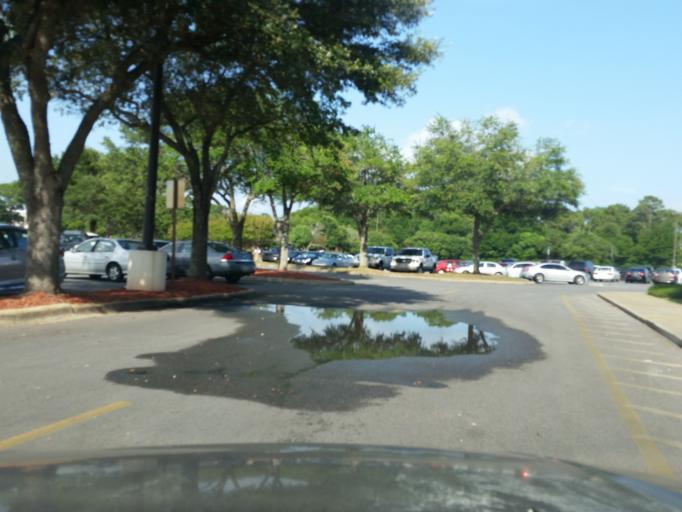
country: US
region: Florida
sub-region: Escambia County
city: Brent
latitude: 30.4763
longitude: -87.2061
